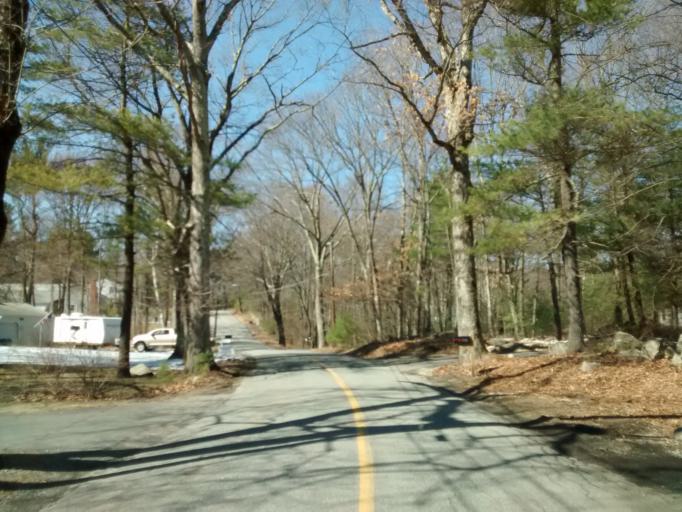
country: US
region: Massachusetts
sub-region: Worcester County
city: Northbridge
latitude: 42.1602
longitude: -71.6878
